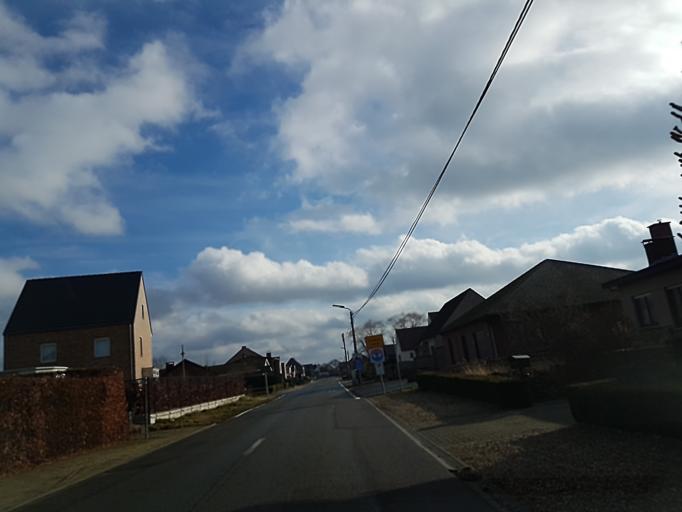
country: BE
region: Flanders
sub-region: Provincie Antwerpen
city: Laakdal
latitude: 51.1032
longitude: 4.9927
